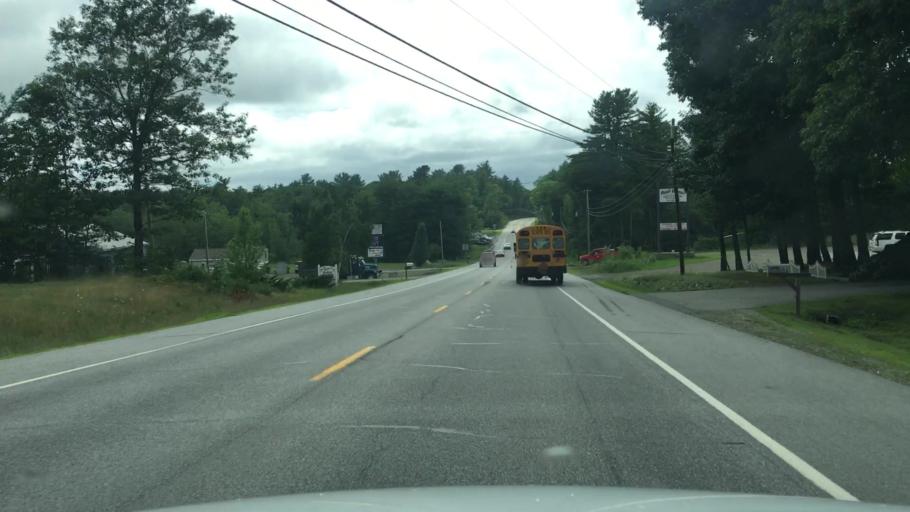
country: US
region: Maine
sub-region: Kennebec County
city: Chelsea
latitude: 44.2746
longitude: -69.6498
